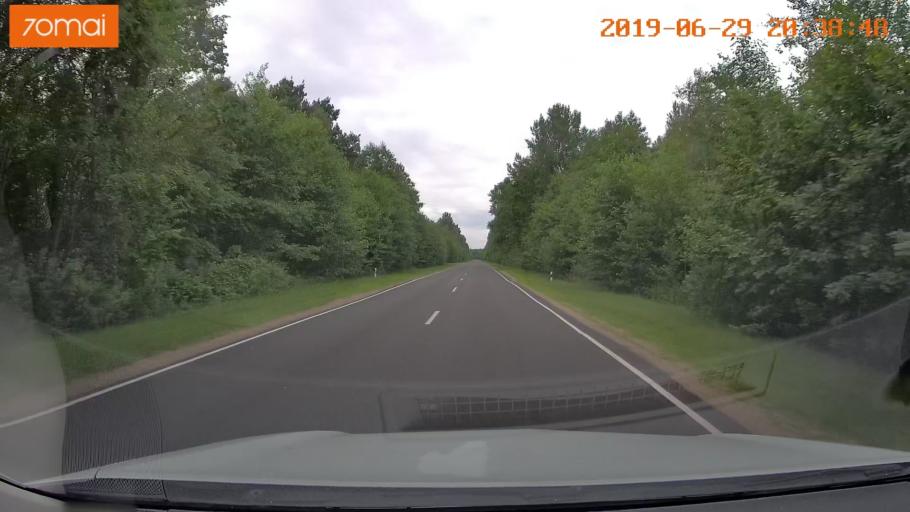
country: BY
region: Brest
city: Hantsavichy
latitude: 52.5544
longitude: 26.3640
